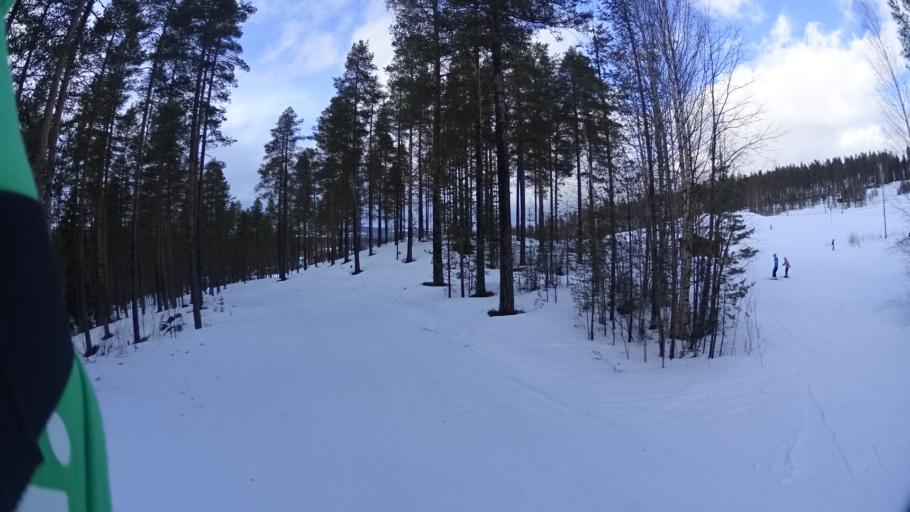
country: SE
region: Vaesterbotten
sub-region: Mala Kommun
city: Mala
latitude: 65.1791
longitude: 18.7531
